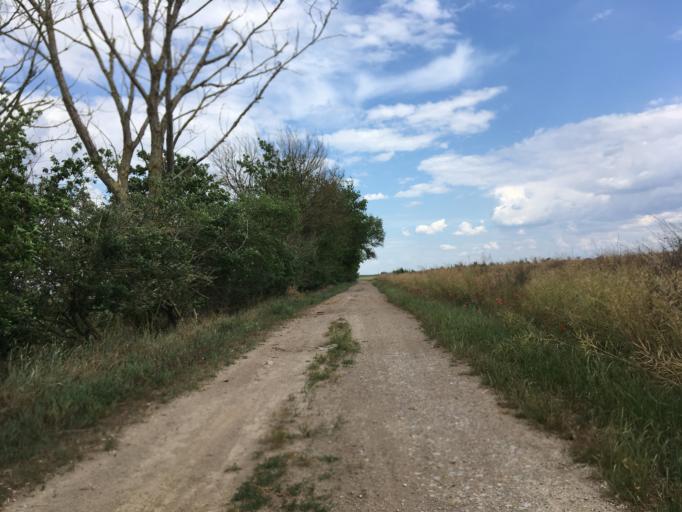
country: DE
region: Saxony-Anhalt
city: Wulfen
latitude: 51.7605
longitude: 11.8936
